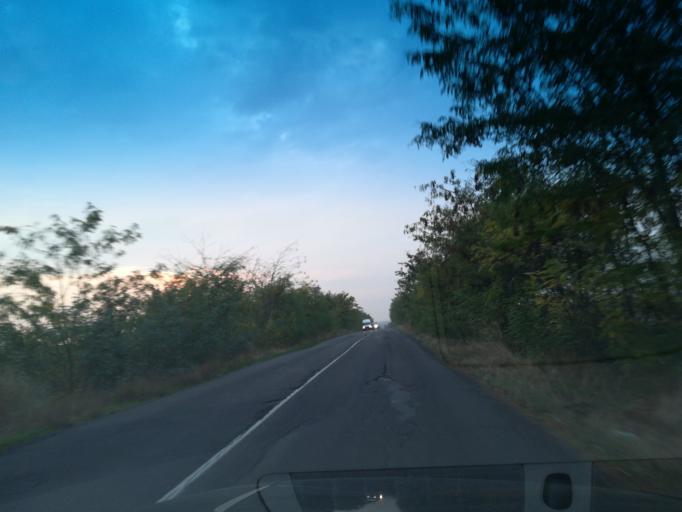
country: BG
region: Stara Zagora
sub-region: Obshtina Chirpan
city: Chirpan
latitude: 42.1800
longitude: 25.2315
